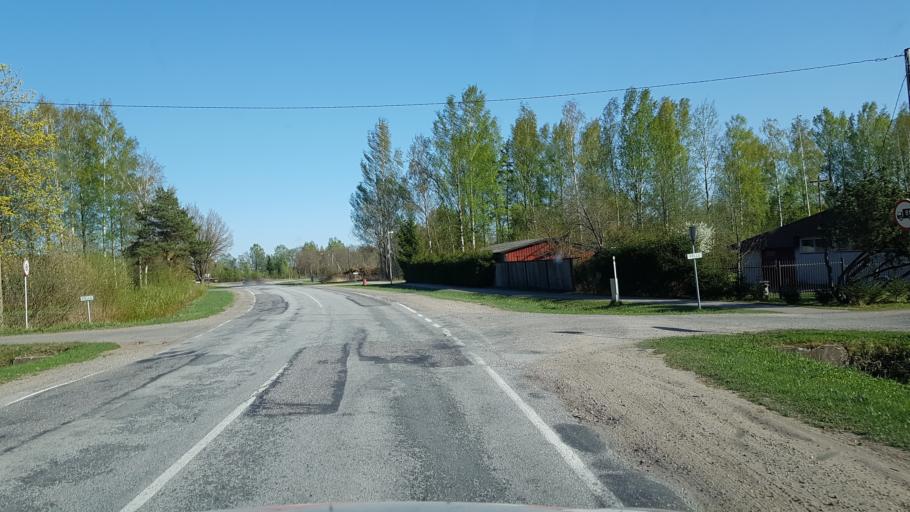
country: EE
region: Paernumaa
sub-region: Paikuse vald
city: Paikuse
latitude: 58.3753
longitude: 24.6241
